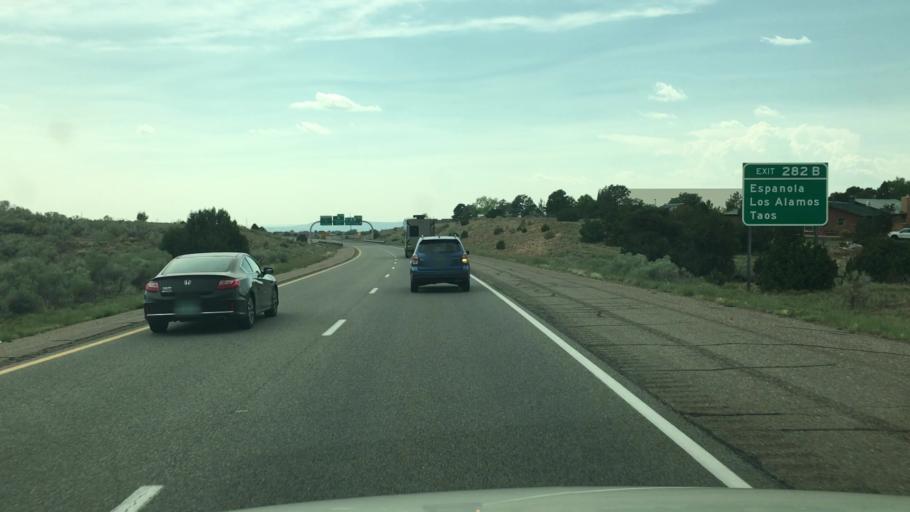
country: US
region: New Mexico
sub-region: Santa Fe County
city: Santa Fe
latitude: 35.6373
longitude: -105.9467
